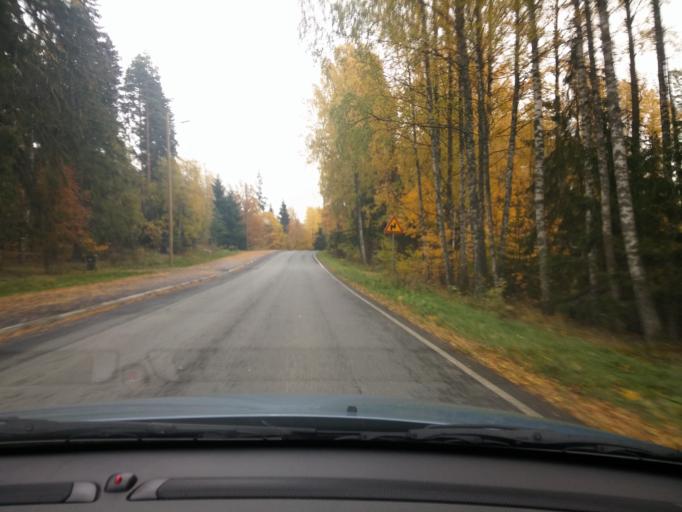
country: FI
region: Haeme
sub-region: Forssa
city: Tammela
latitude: 60.8043
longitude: 23.8023
